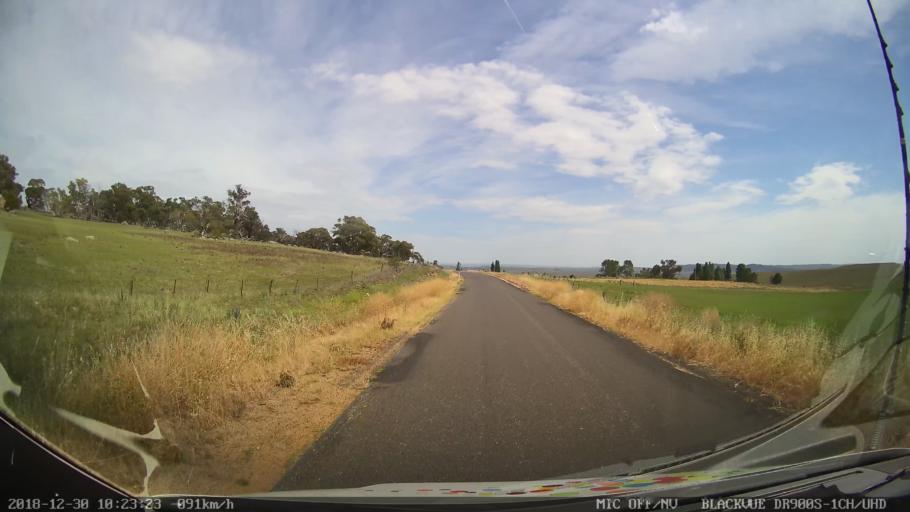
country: AU
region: New South Wales
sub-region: Snowy River
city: Berridale
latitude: -36.5382
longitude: 148.9825
